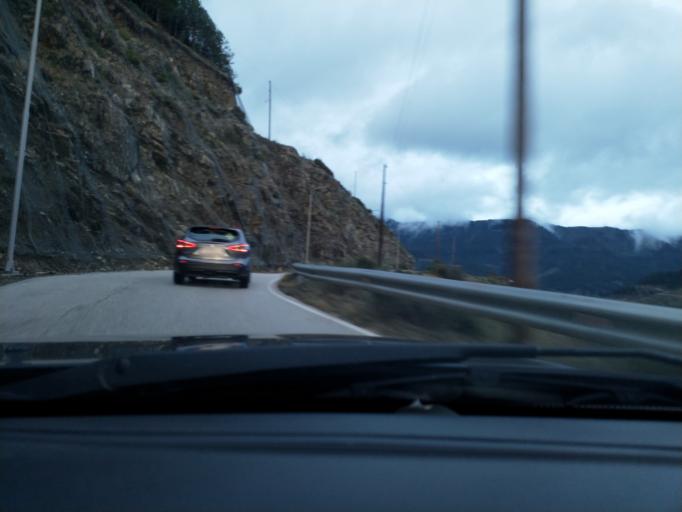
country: GR
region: Epirus
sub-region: Nomos Ioanninon
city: Metsovo
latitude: 39.7646
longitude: 21.1765
